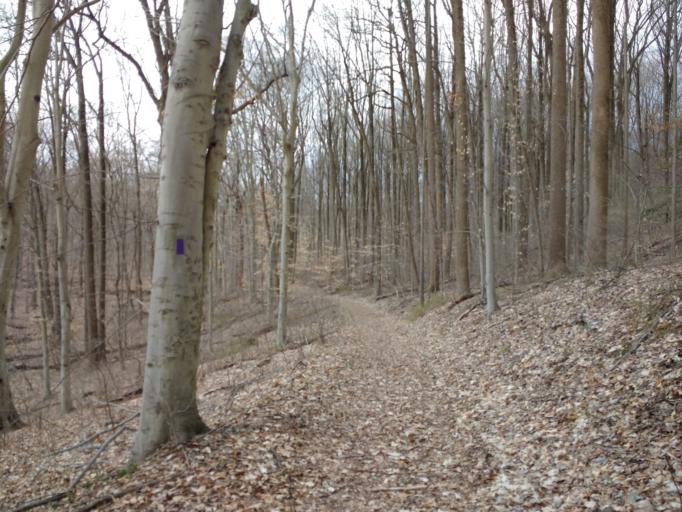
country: US
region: Pennsylvania
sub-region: Delaware County
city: Lima
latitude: 39.9418
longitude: -75.4282
